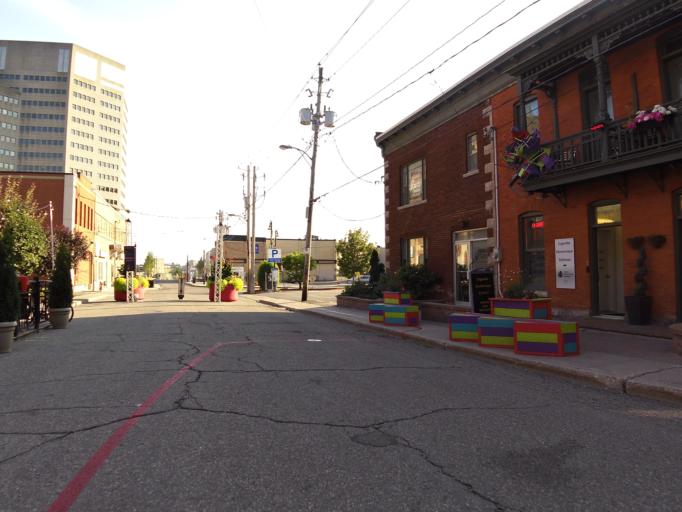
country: CA
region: Ontario
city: Ottawa
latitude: 45.4268
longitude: -75.7163
